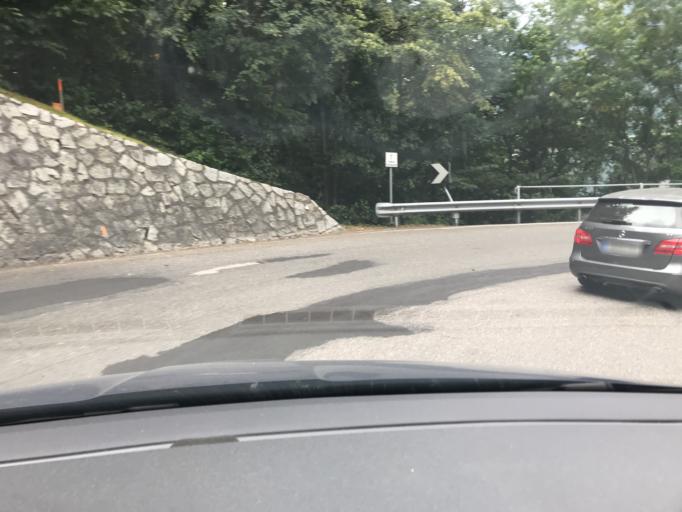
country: IT
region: Trentino-Alto Adige
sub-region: Bolzano
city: Bressanone
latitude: 46.6945
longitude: 11.6591
